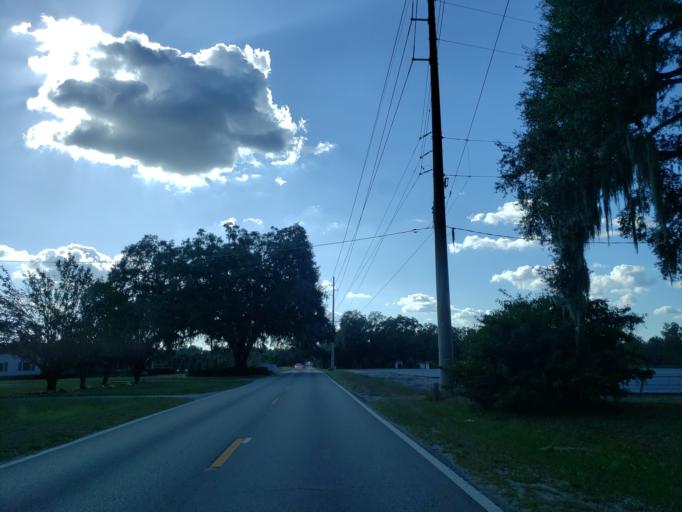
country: US
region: Florida
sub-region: Hillsborough County
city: Dover
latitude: 27.9670
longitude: -82.2119
